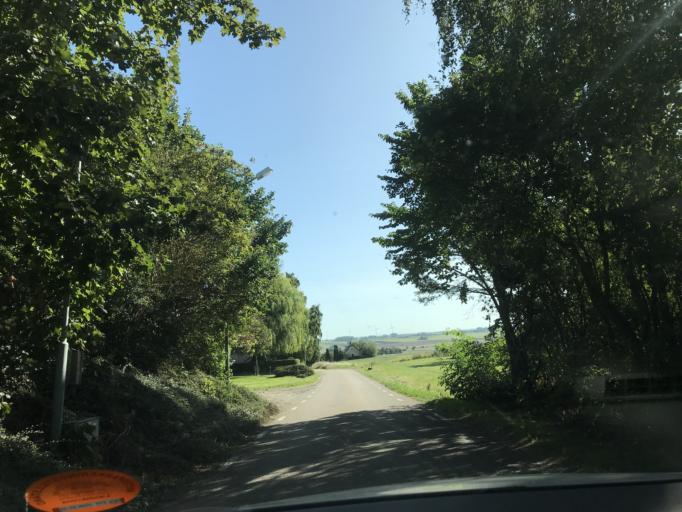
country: SE
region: Skane
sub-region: Landskrona
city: Asmundtorp
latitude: 55.9075
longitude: 12.9443
